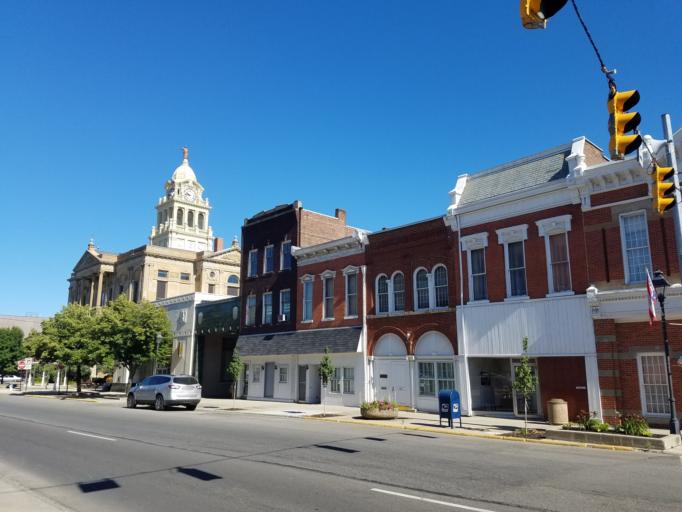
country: US
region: Ohio
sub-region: Marion County
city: Marion
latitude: 40.5888
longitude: -83.1277
